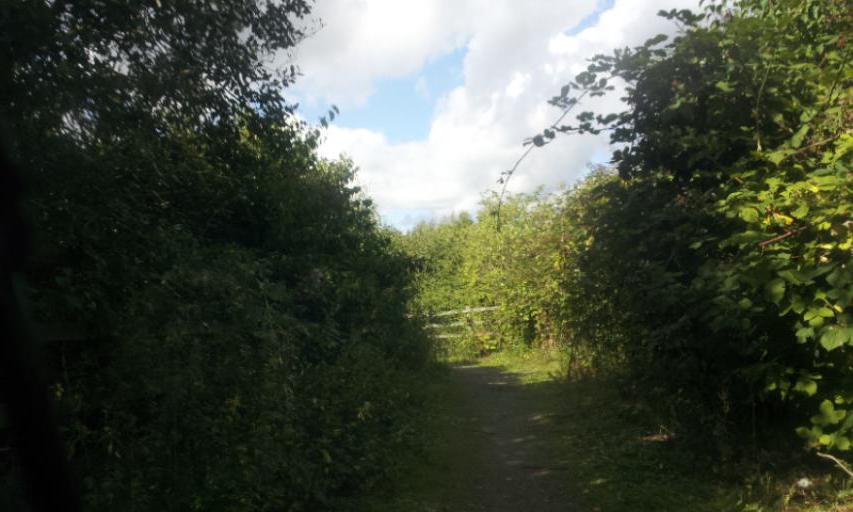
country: GB
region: England
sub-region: Kent
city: West Malling
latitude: 51.3042
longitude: 0.4147
